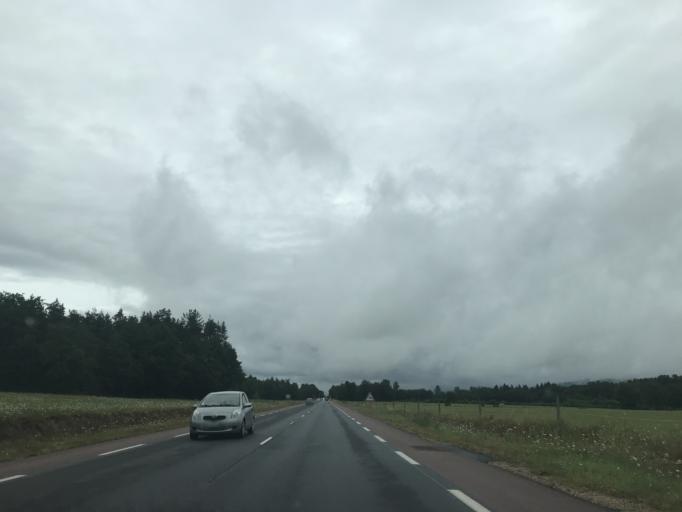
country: FR
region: Auvergne
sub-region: Departement du Puy-de-Dome
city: Arlanc
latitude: 45.4436
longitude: 3.7240
